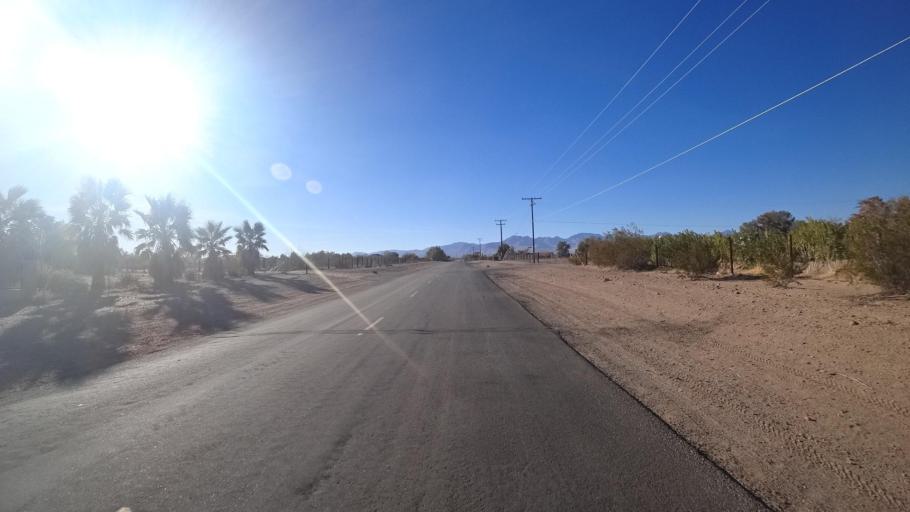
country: US
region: California
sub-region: Kern County
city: Ridgecrest
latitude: 35.6298
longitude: -117.7123
